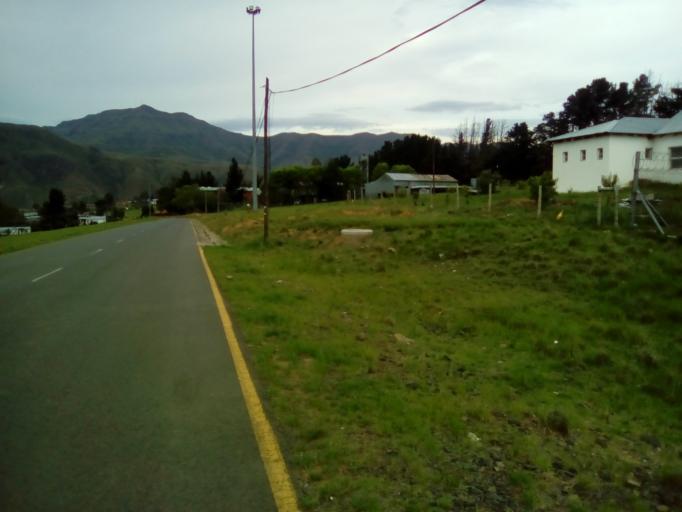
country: LS
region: Qacha's Nek
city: Qacha's Nek
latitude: -30.1140
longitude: 28.6805
